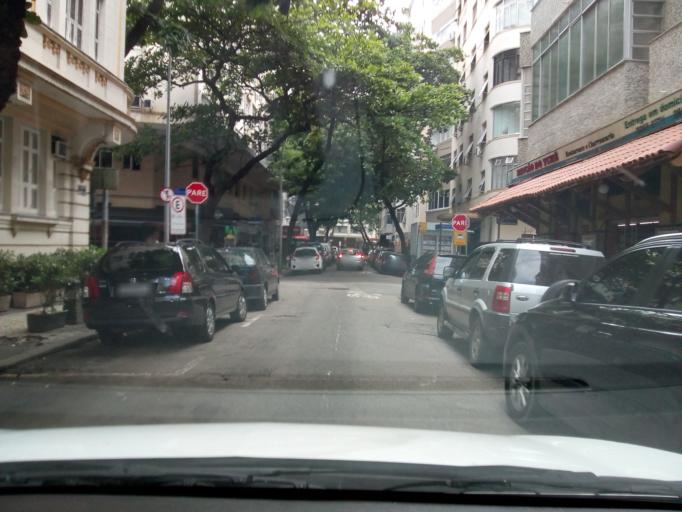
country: BR
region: Rio de Janeiro
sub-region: Rio De Janeiro
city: Rio de Janeiro
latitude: -22.9749
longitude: -43.1883
